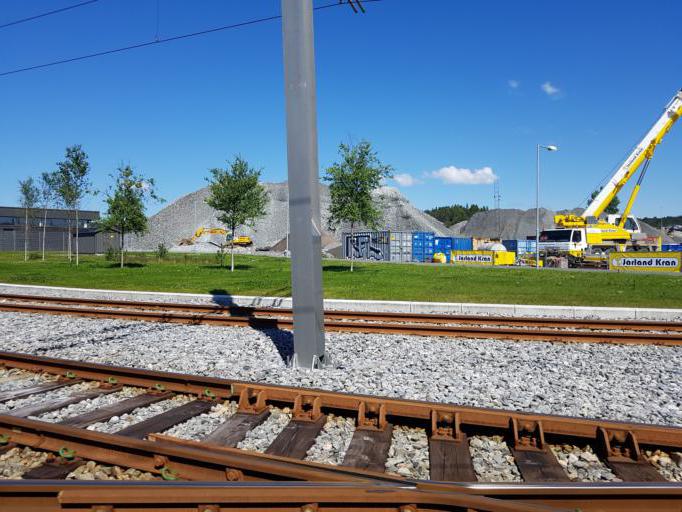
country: NO
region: Hordaland
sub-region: Bergen
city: Ytrebygda
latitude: 60.2918
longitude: 5.2448
